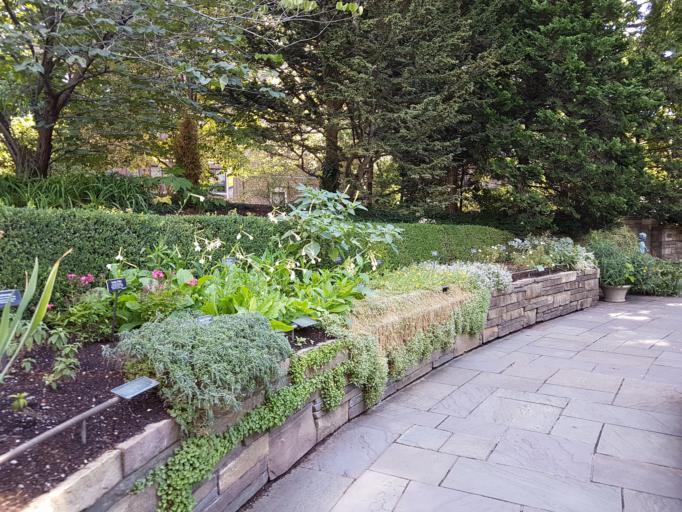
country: US
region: New York
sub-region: Kings County
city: Brooklyn
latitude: 40.6682
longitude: -73.9623
